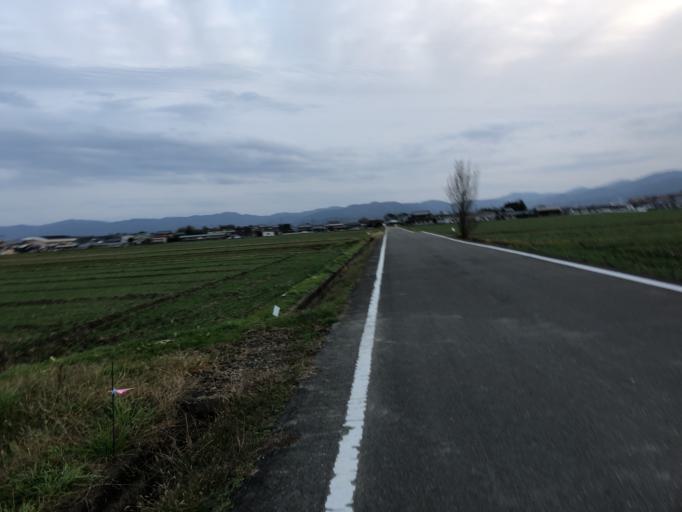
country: JP
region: Kyoto
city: Kameoka
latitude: 35.0620
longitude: 135.5618
